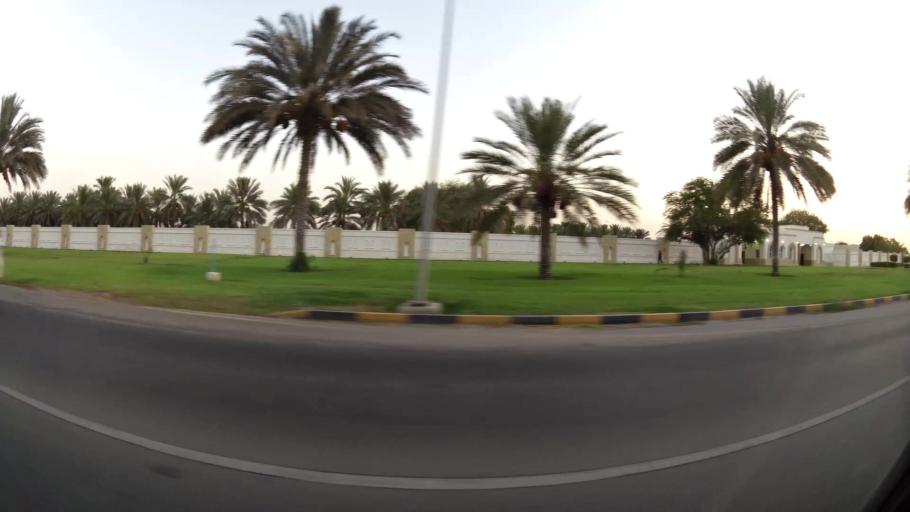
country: OM
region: Muhafazat Masqat
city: As Sib al Jadidah
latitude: 23.6518
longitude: 58.2119
